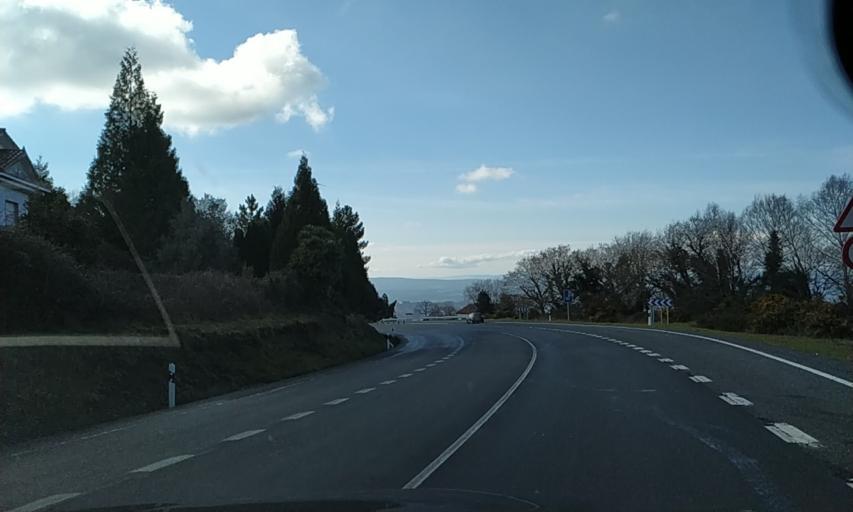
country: ES
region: Galicia
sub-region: Provincia da Coruna
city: Ribeira
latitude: 42.7144
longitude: -8.3738
